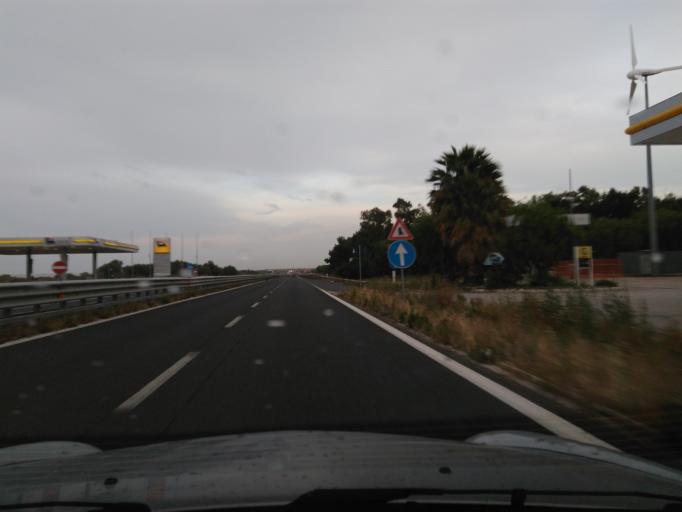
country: IT
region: Apulia
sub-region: Provincia di Bari
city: Giovinazzo
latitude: 41.1676
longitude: 16.7035
